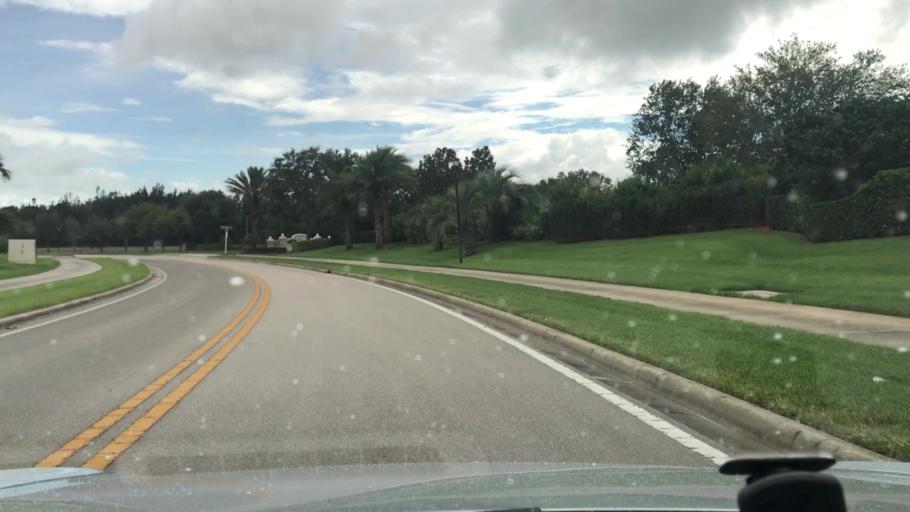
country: US
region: Florida
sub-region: Indian River County
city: Gifford
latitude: 27.6857
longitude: -80.4388
